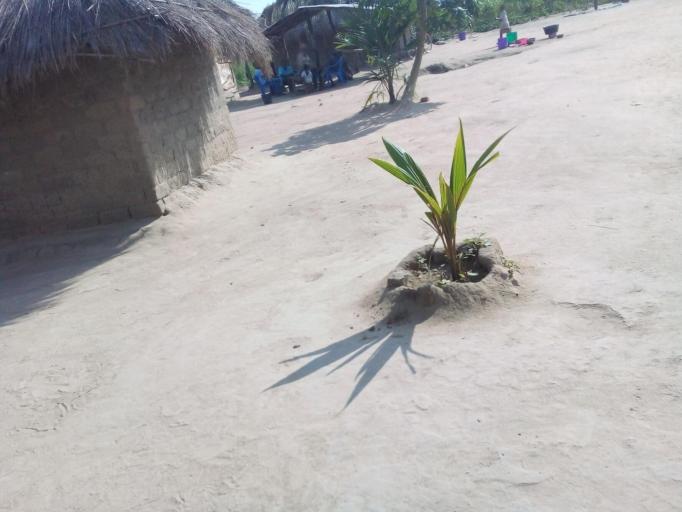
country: MZ
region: Zambezia
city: Quelimane
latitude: -17.5520
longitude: 36.7075
